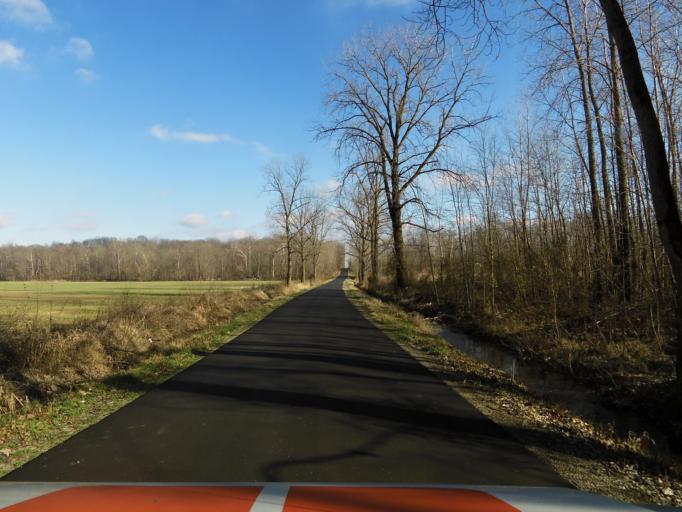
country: US
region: Indiana
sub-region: Jackson County
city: Seymour
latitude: 38.9830
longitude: -85.7900
